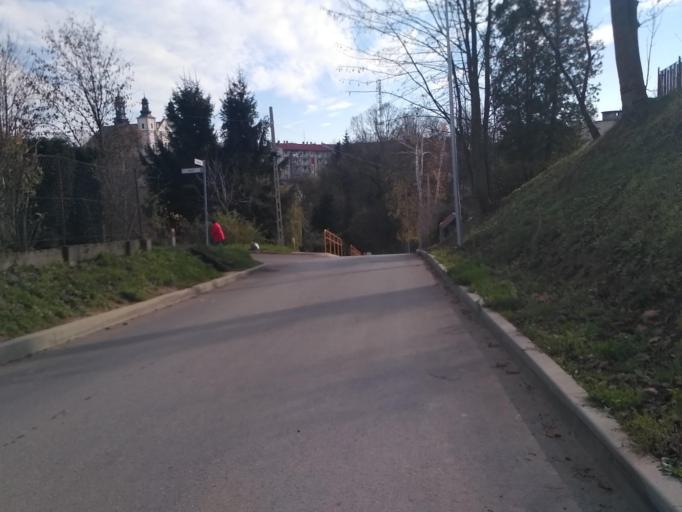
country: PL
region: Subcarpathian Voivodeship
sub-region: Powiat brzozowski
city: Brzozow
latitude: 49.6967
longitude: 22.0161
